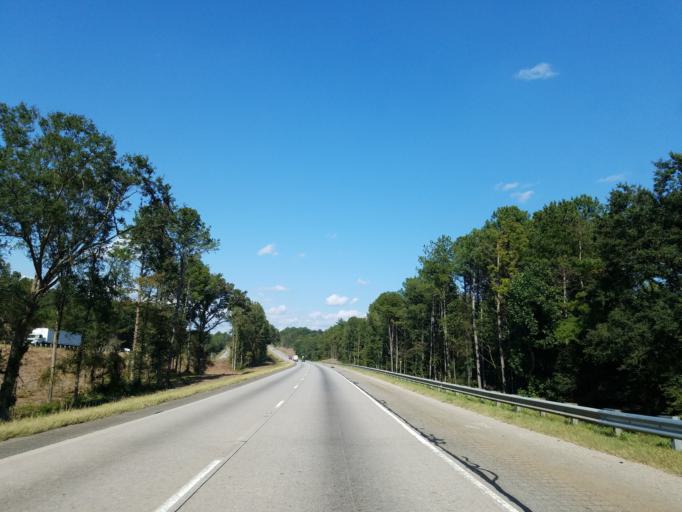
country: US
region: Georgia
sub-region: Jackson County
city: Commerce
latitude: 34.2705
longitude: -83.4393
